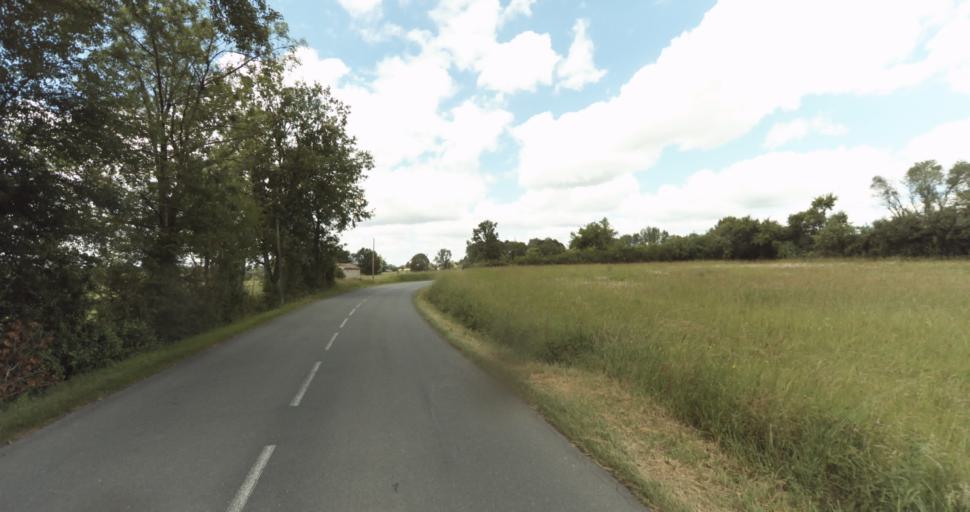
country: FR
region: Aquitaine
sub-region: Departement du Lot-et-Garonne
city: Villereal
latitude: 44.6862
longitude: 0.7555
